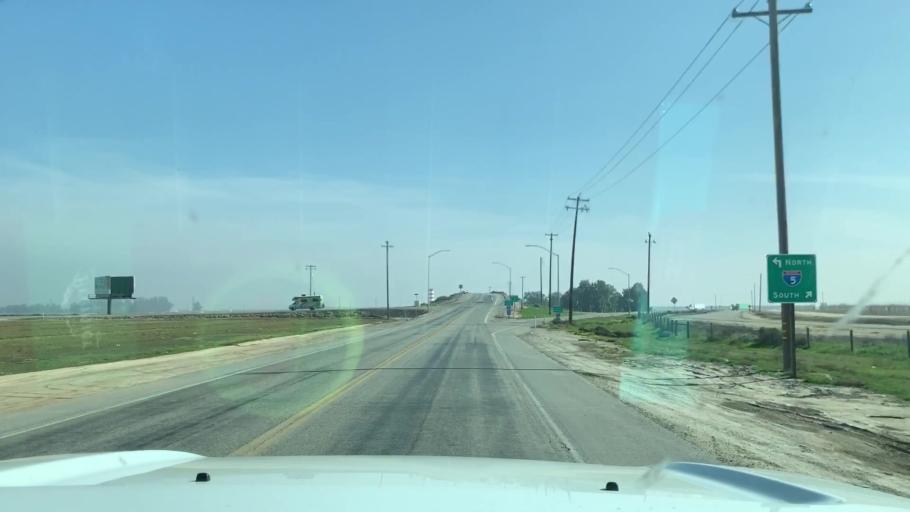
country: US
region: California
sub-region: Kern County
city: Buttonwillow
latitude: 35.4424
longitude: -119.4607
